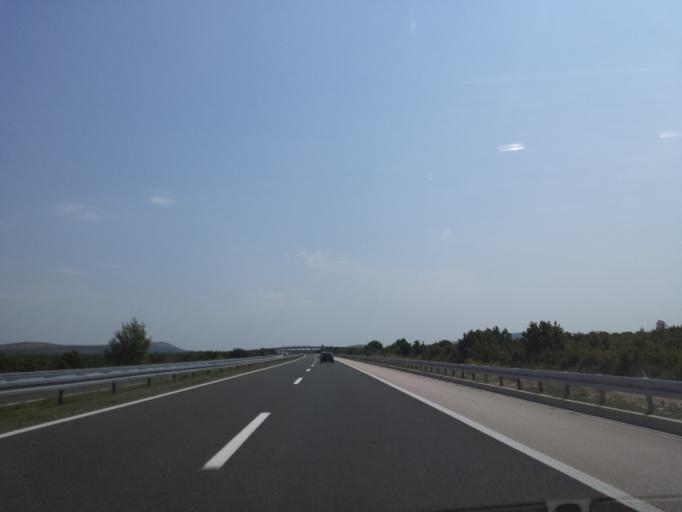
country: HR
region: Zadarska
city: Benkovac
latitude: 43.9667
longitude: 15.6539
